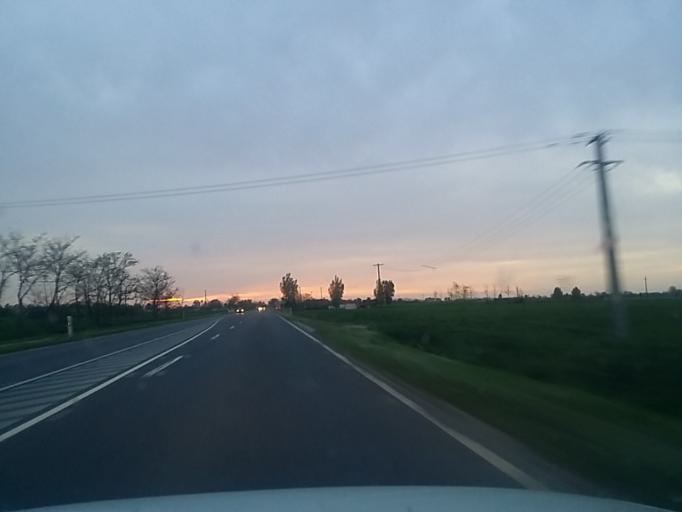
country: HU
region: Bekes
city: Kondoros
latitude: 46.7289
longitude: 20.9127
